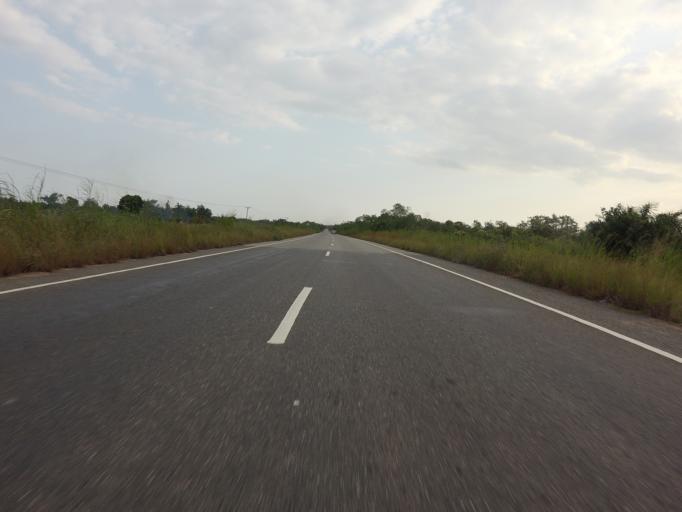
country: GH
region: Volta
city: Ho
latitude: 6.1324
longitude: 0.5243
